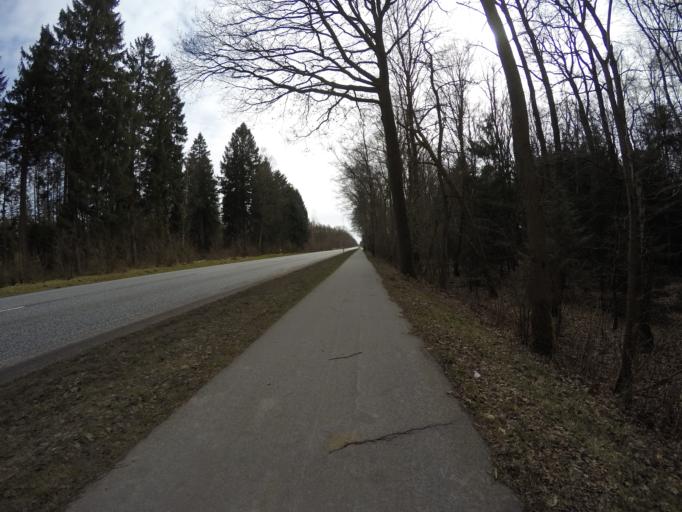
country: DE
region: Schleswig-Holstein
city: Heidmoor
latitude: 53.8325
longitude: 9.8840
